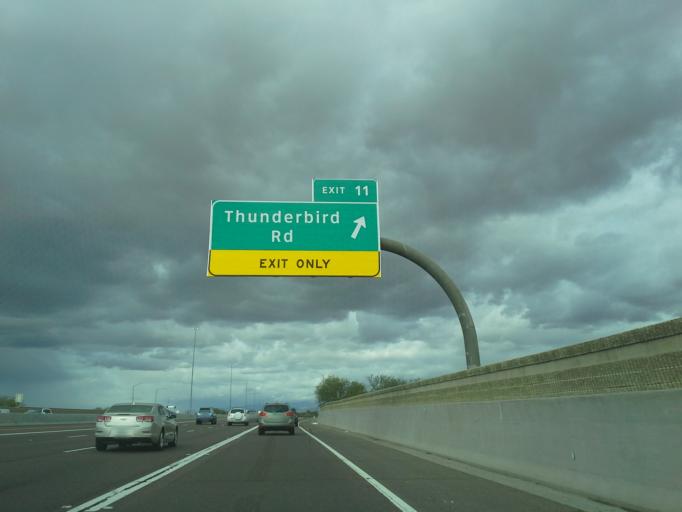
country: US
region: Arizona
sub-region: Maricopa County
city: Paradise Valley
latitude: 33.6051
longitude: -112.0093
